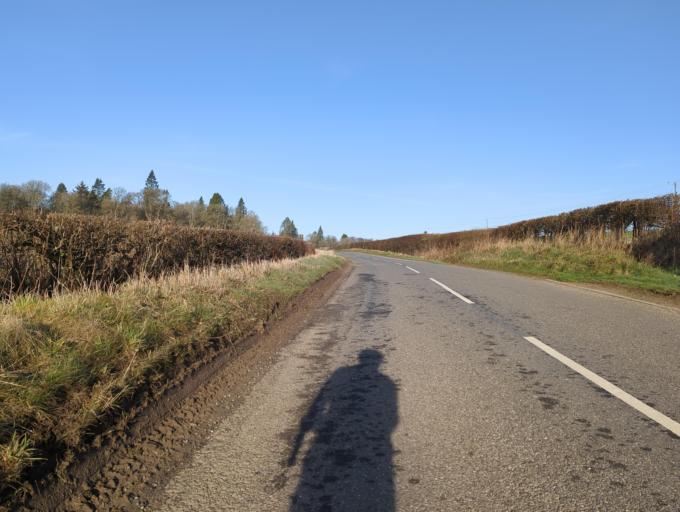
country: GB
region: Scotland
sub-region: Perth and Kinross
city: Methven
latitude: 56.4535
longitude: -3.5376
